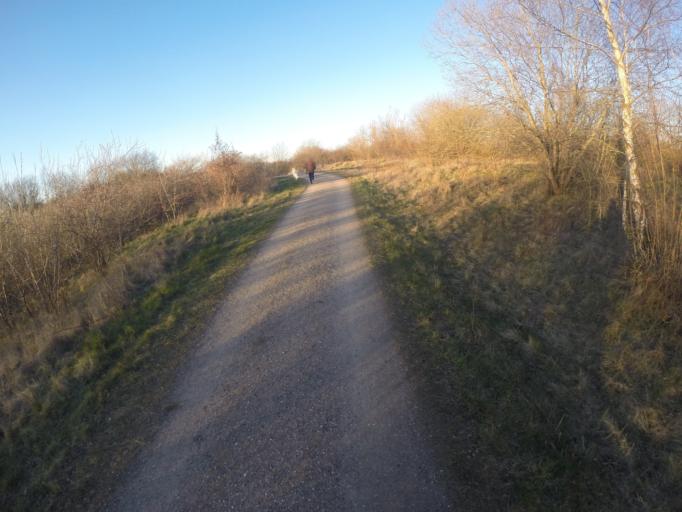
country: DK
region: Capital Region
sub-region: Hoje-Taastrup Kommune
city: Flong
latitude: 55.6365
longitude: 12.1870
